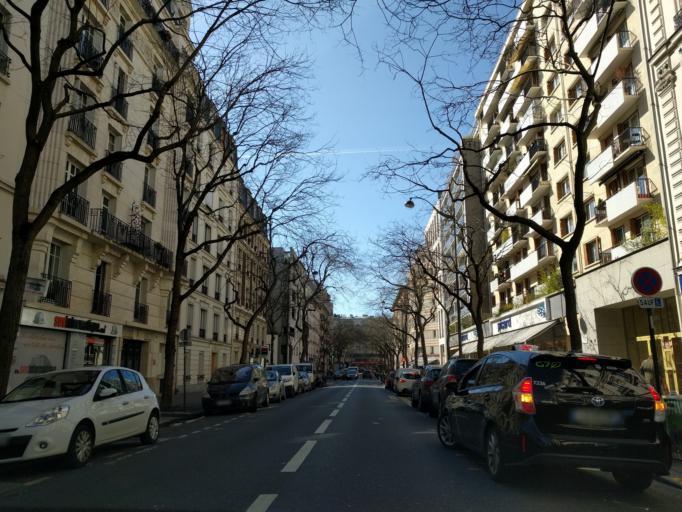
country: FR
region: Ile-de-France
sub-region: Departement du Val-de-Marne
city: Saint-Mande
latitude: 48.8384
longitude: 2.4039
